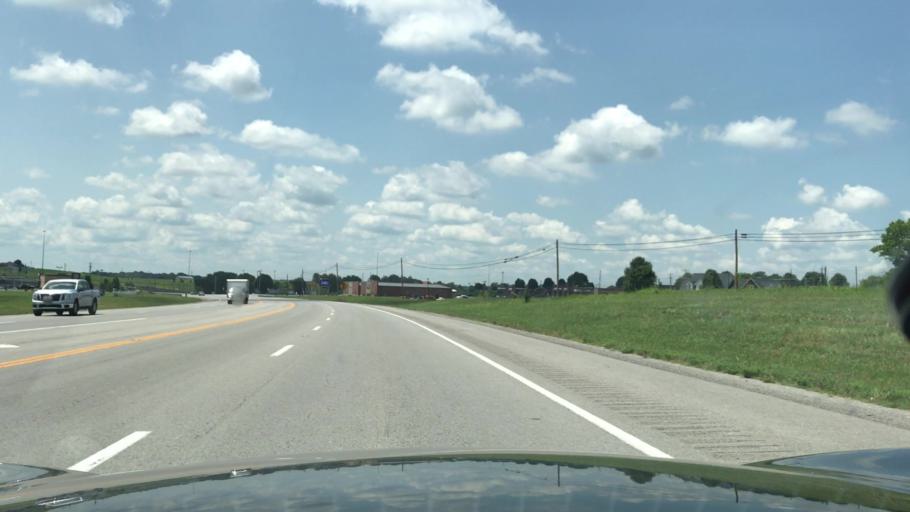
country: US
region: Kentucky
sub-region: Adair County
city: Columbia
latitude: 37.0790
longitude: -85.3357
